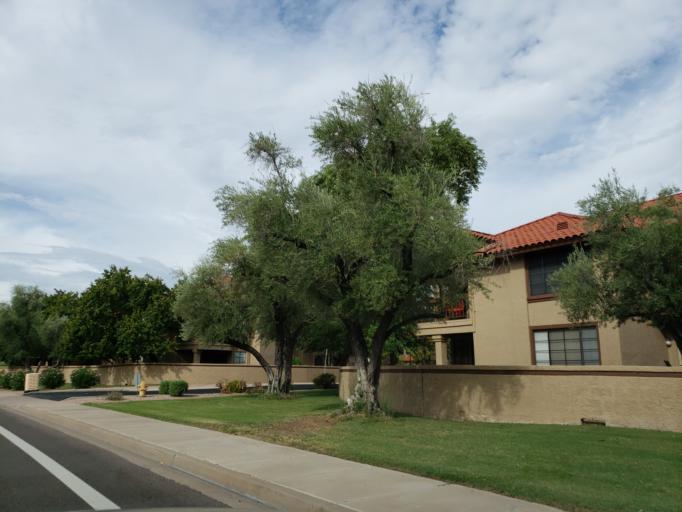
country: US
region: Arizona
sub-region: Maricopa County
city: Scottsdale
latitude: 33.5746
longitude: -111.8915
